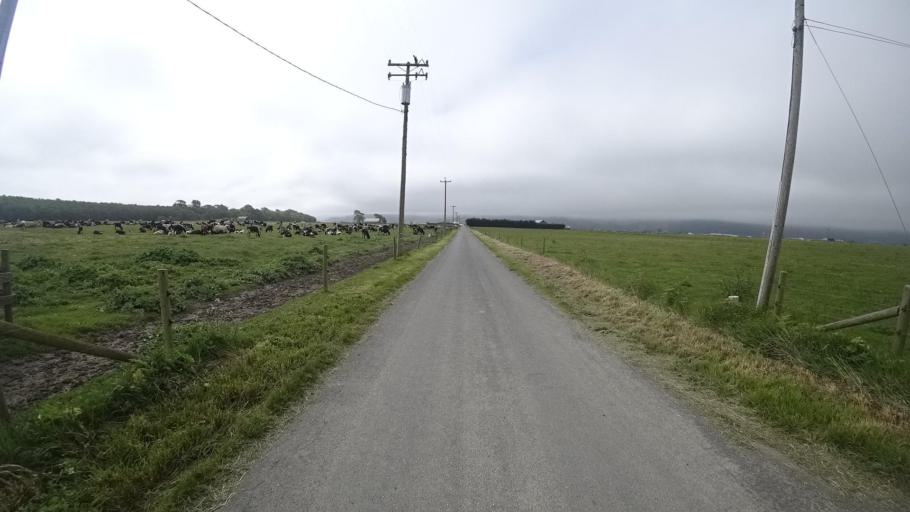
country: US
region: California
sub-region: Humboldt County
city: Fortuna
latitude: 40.5887
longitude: -124.1879
